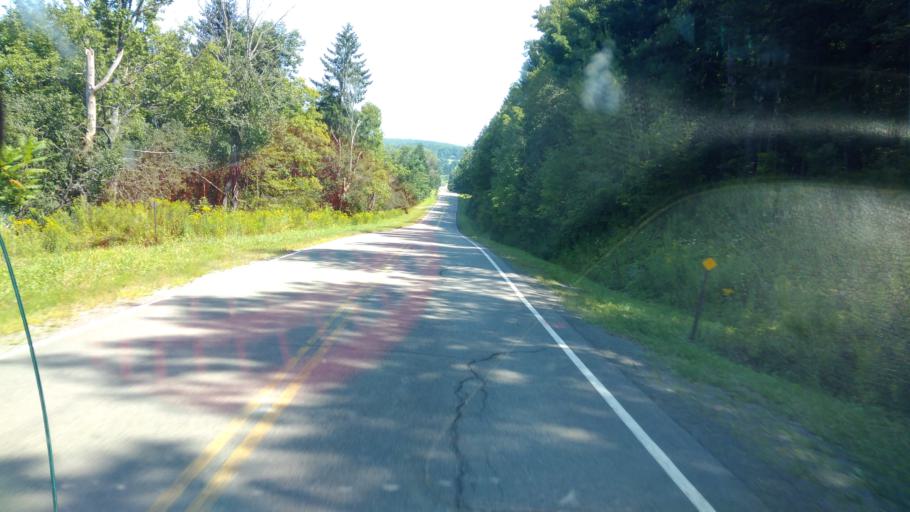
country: US
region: New York
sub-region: Allegany County
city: Alfred
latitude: 42.2978
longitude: -77.8934
